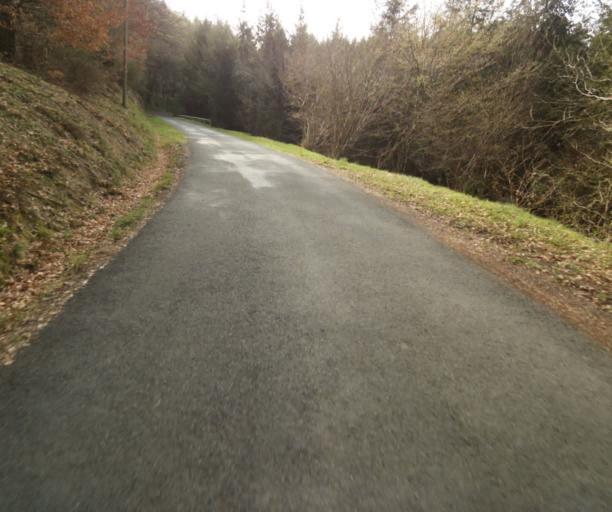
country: FR
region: Limousin
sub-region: Departement de la Correze
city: Correze
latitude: 45.4245
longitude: 1.8015
